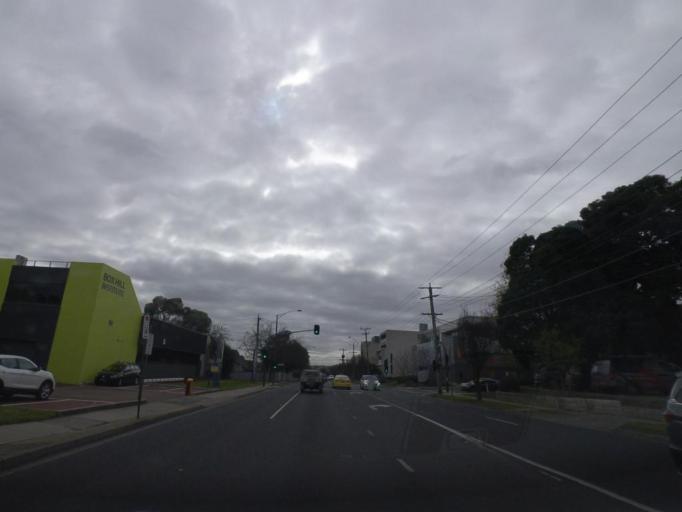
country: AU
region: Victoria
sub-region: Whitehorse
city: Box Hill
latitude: -37.8144
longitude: 145.1155
